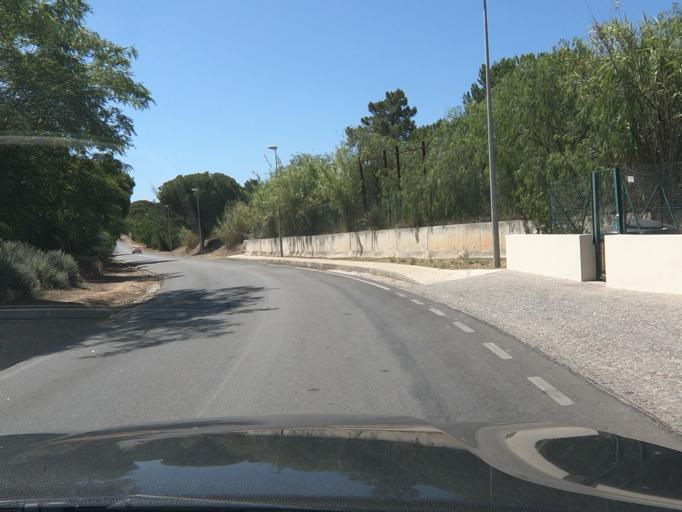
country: PT
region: Faro
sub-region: Loule
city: Vilamoura
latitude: 37.0923
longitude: -8.1029
